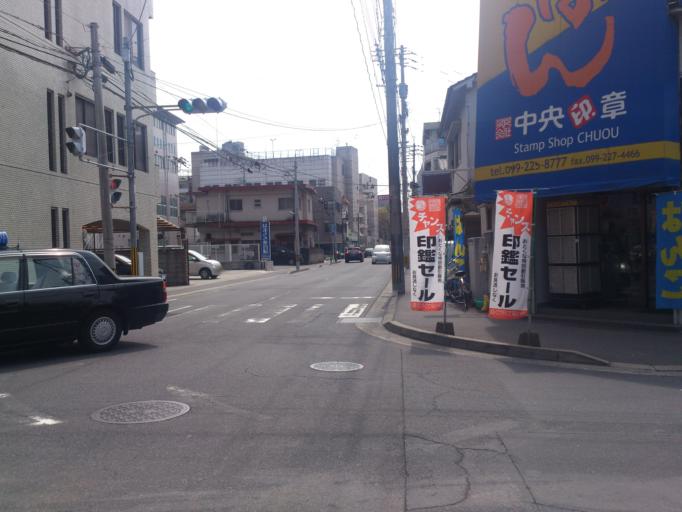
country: JP
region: Kagoshima
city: Kagoshima-shi
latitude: 31.5862
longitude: 130.5512
